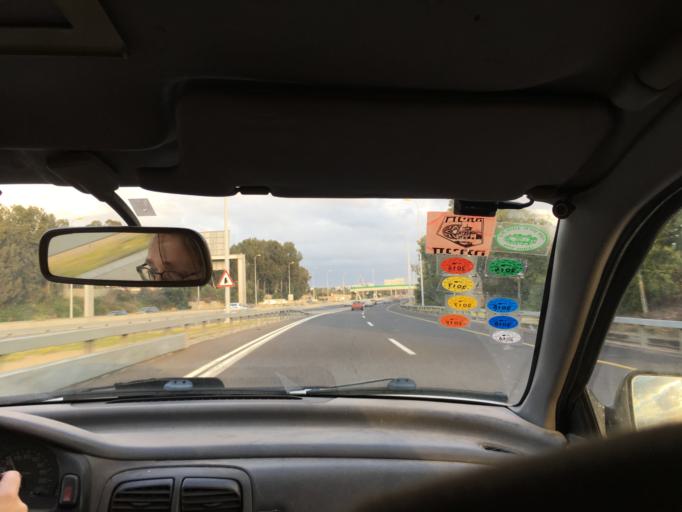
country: IL
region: Tel Aviv
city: Ramat HaSharon
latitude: 32.1383
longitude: 34.8139
